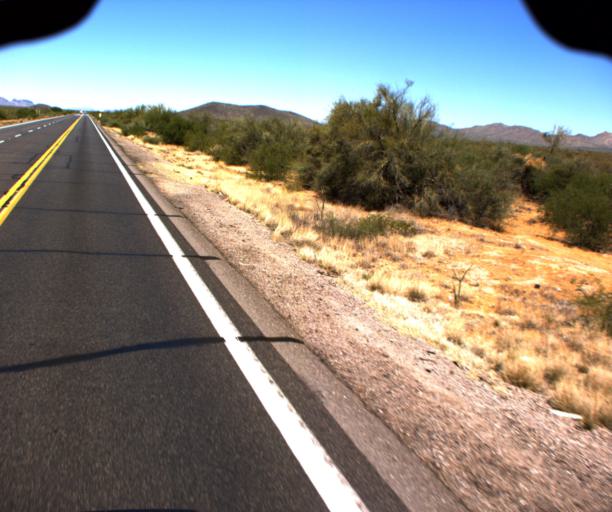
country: US
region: Arizona
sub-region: Yavapai County
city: Congress
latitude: 34.1508
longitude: -112.9899
